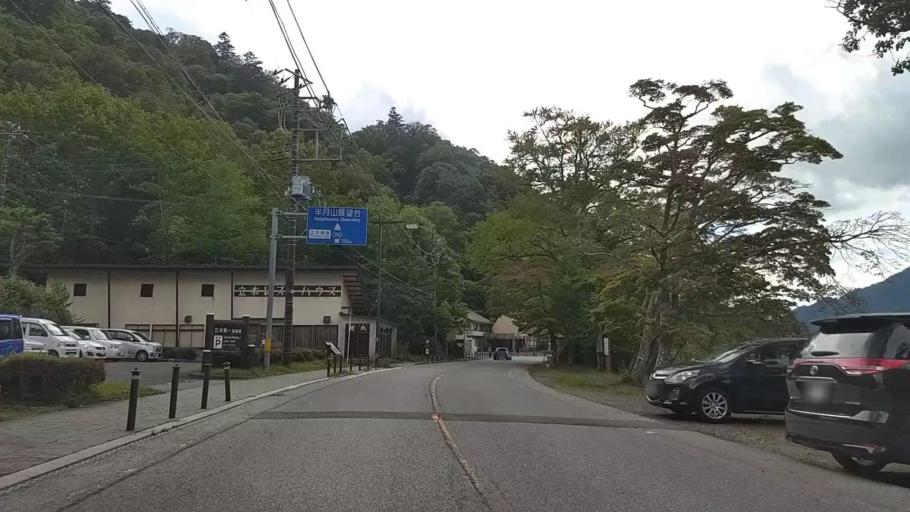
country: JP
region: Tochigi
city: Nikko
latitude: 36.7362
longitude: 139.4957
